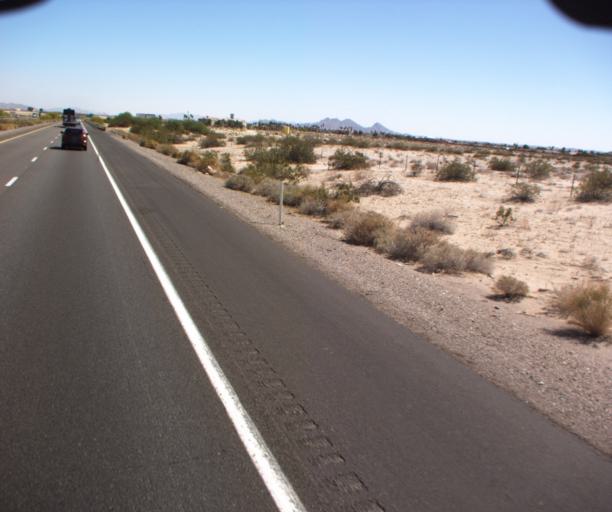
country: US
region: Arizona
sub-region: Yuma County
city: Wellton
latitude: 32.6590
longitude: -114.1535
